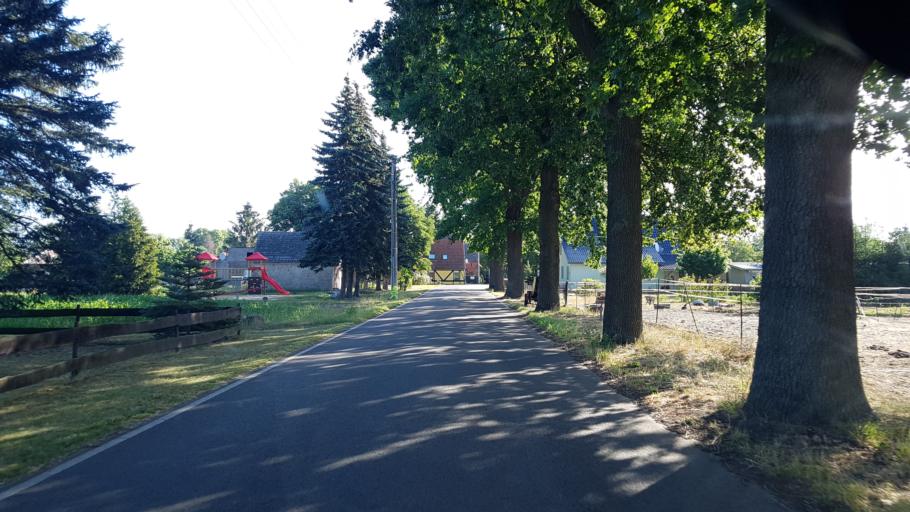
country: DE
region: Brandenburg
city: Kasel-Golzig
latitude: 51.9580
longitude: 13.6689
